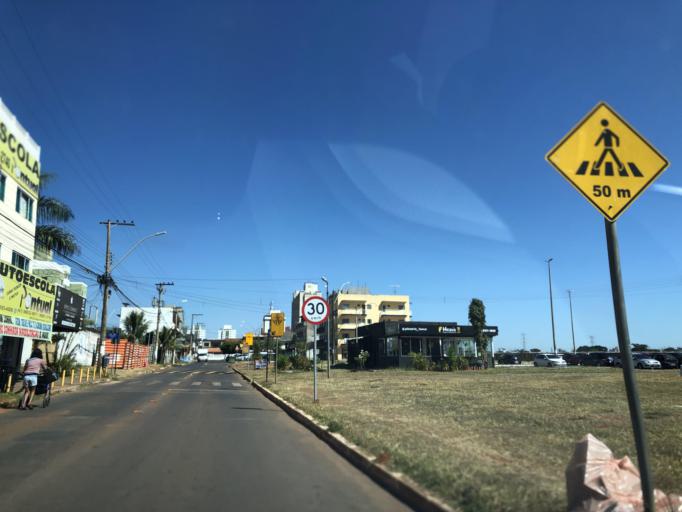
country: BR
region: Federal District
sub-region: Brasilia
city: Brasilia
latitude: -15.8656
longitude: -48.0589
